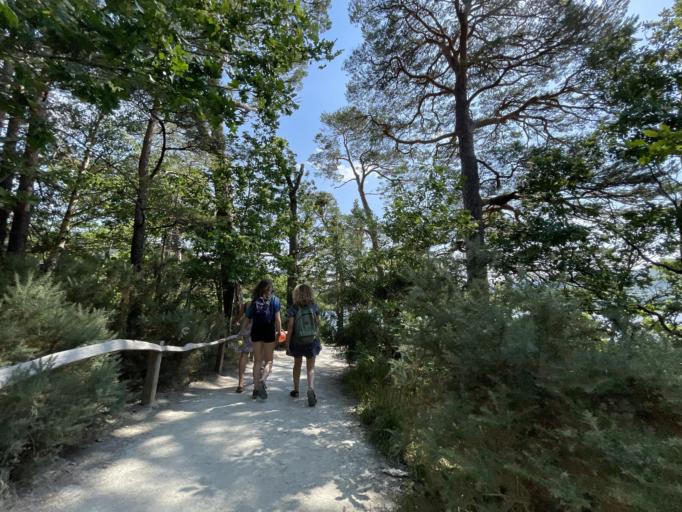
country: GB
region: England
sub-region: Cumbria
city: Keswick
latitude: 54.5902
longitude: -3.1408
